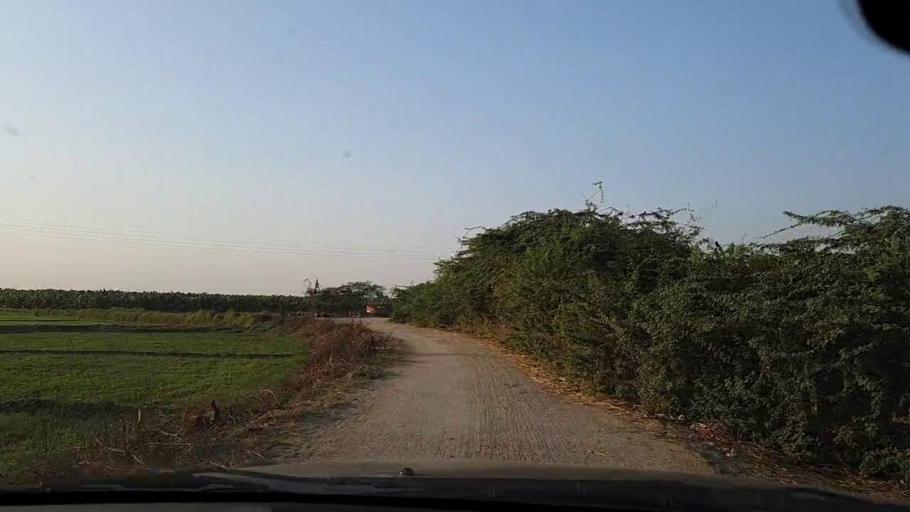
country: PK
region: Sindh
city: Thatta
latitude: 24.5633
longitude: 67.8788
